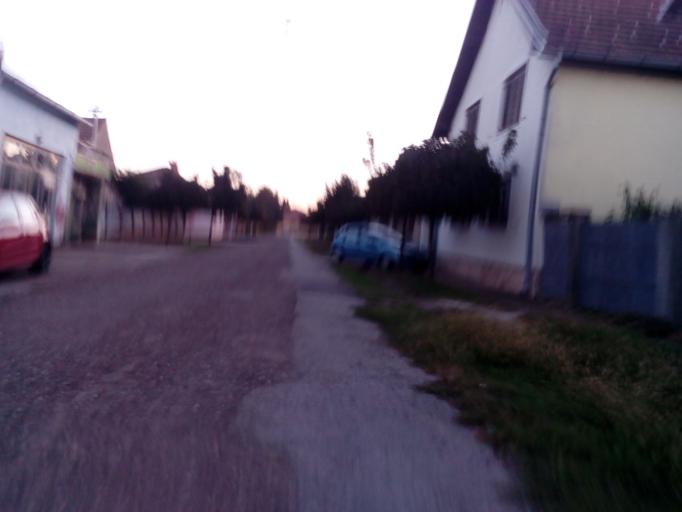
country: HR
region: Vukovarsko-Srijemska
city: Vinkovci
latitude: 45.3010
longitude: 18.8129
